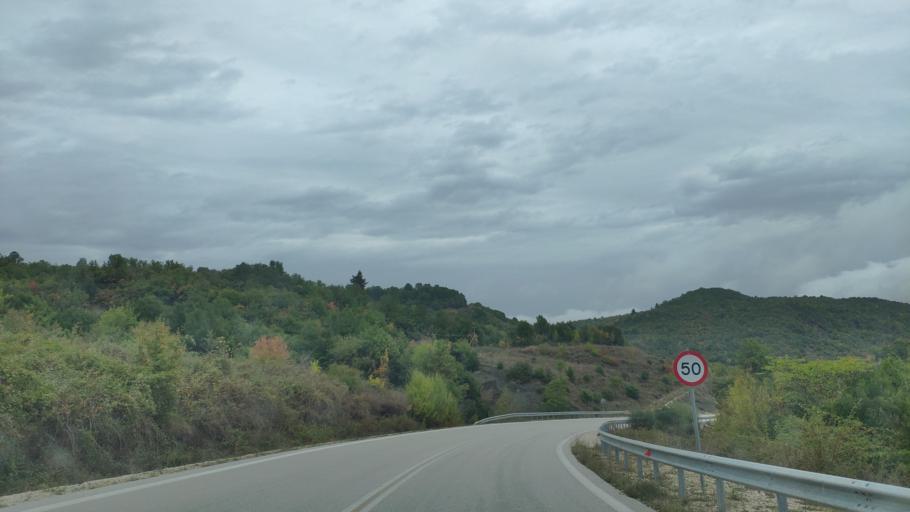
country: GR
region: Epirus
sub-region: Nomos Thesprotias
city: Paramythia
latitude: 39.5003
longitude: 20.6766
